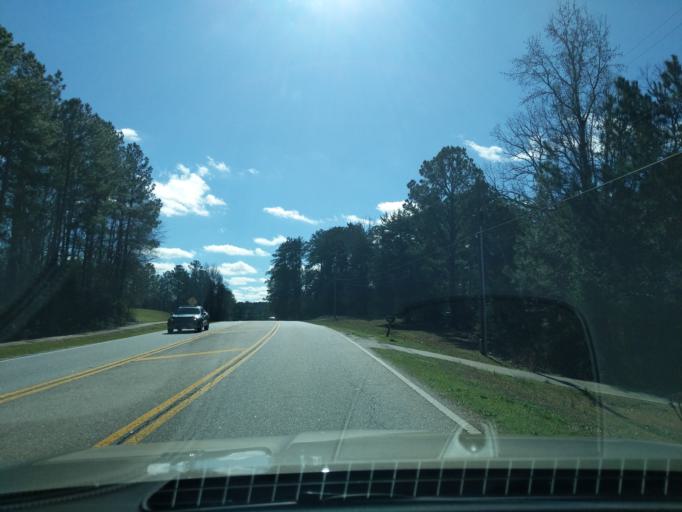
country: US
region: Georgia
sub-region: Columbia County
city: Grovetown
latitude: 33.5161
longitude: -82.2024
